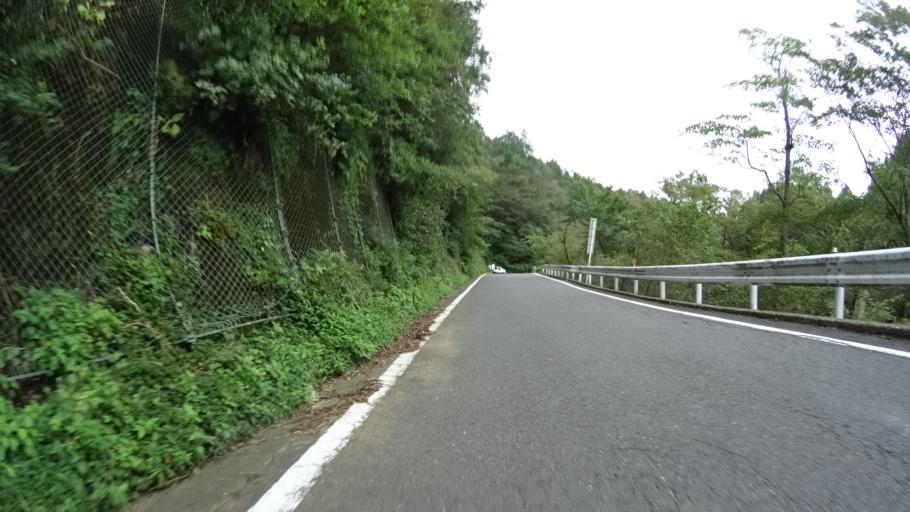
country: JP
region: Kanagawa
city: Hadano
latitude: 35.4271
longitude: 139.2212
